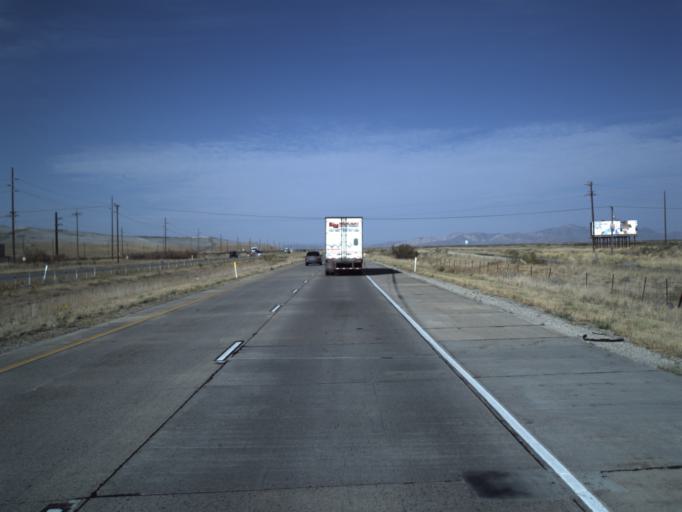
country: US
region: Utah
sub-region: Salt Lake County
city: Magna
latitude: 40.7711
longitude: -112.0972
